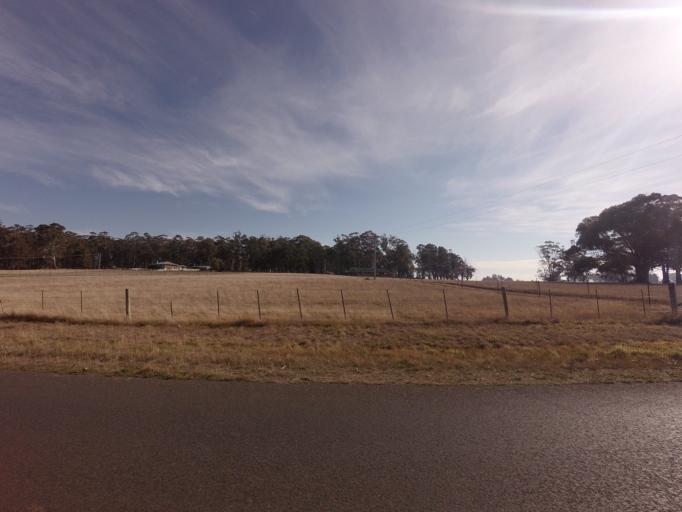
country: AU
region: Tasmania
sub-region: Sorell
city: Sorell
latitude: -42.4623
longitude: 147.4613
